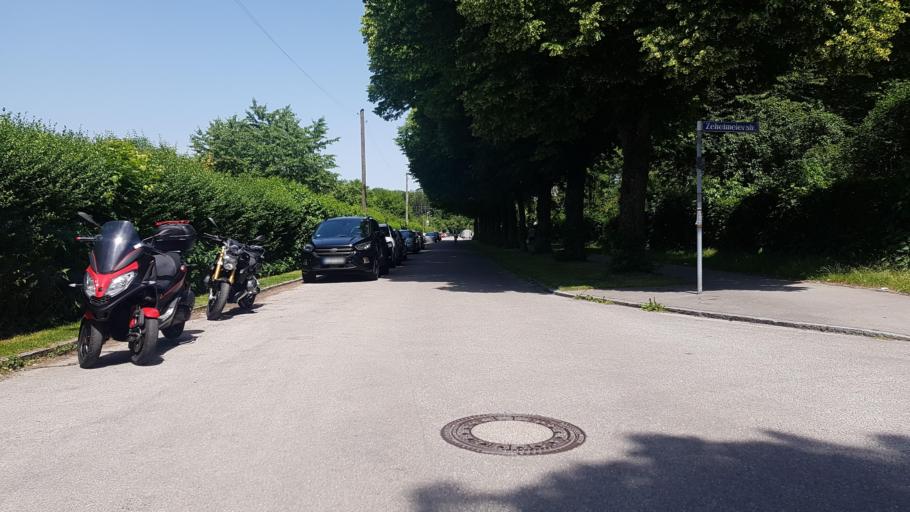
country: DE
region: Bavaria
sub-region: Upper Bavaria
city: Unterfoehring
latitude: 48.1942
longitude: 11.6273
